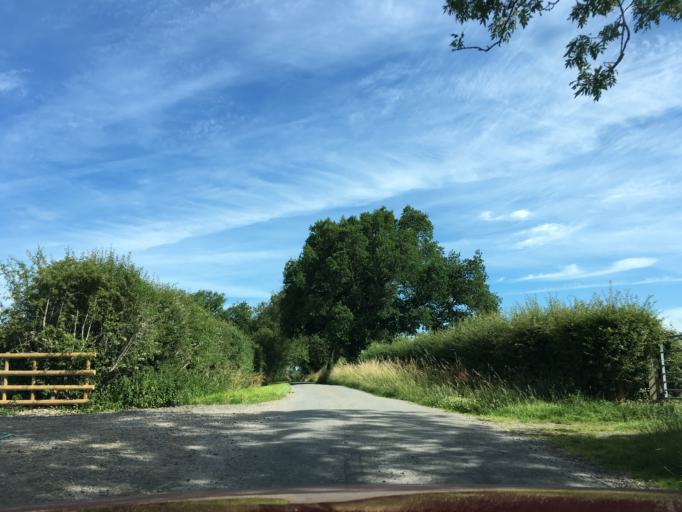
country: GB
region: England
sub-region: South Gloucestershire
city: Horton
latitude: 51.5375
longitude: -2.3612
